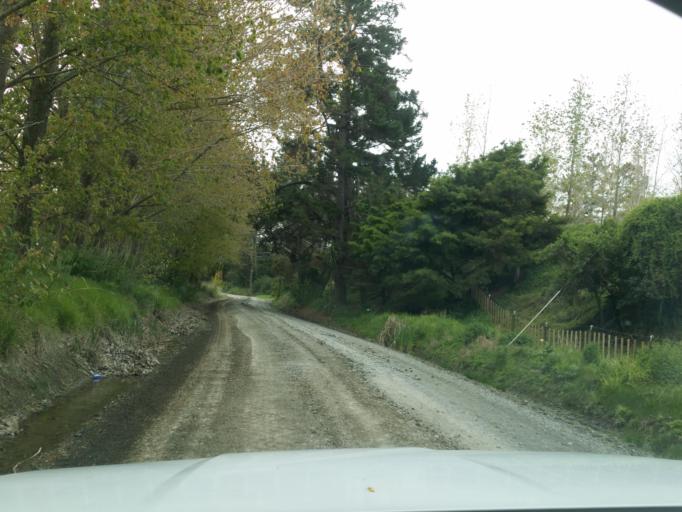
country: NZ
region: Northland
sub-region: Kaipara District
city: Dargaville
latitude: -35.9184
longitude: 173.9215
